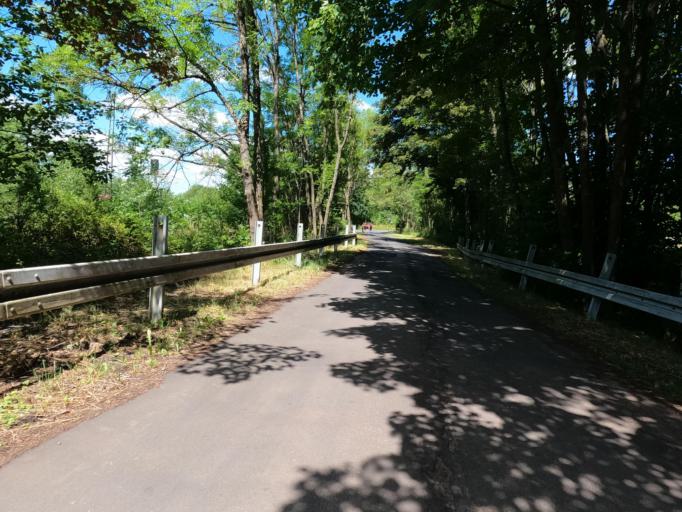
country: DE
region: Hesse
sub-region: Regierungsbezirk Darmstadt
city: Schluchtern
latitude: 50.3394
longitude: 9.6080
